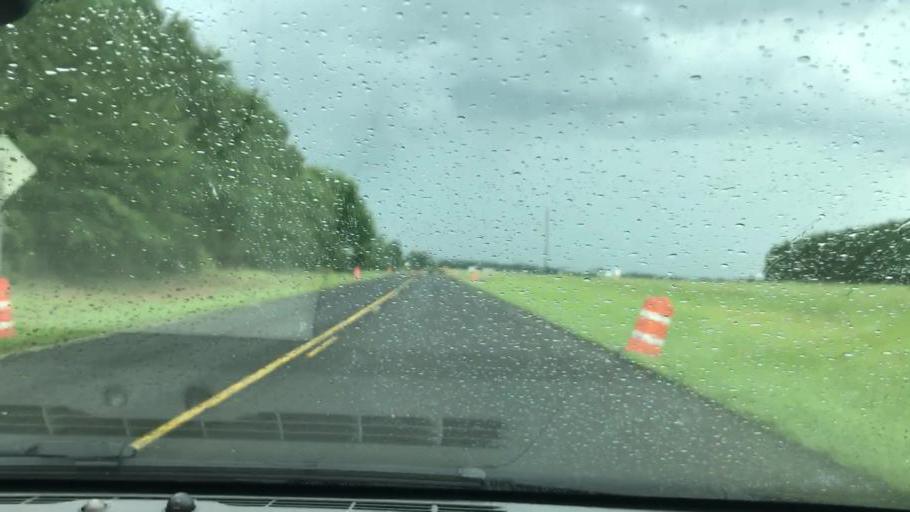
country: US
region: Georgia
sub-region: Clay County
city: Fort Gaines
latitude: 31.4900
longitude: -85.0174
